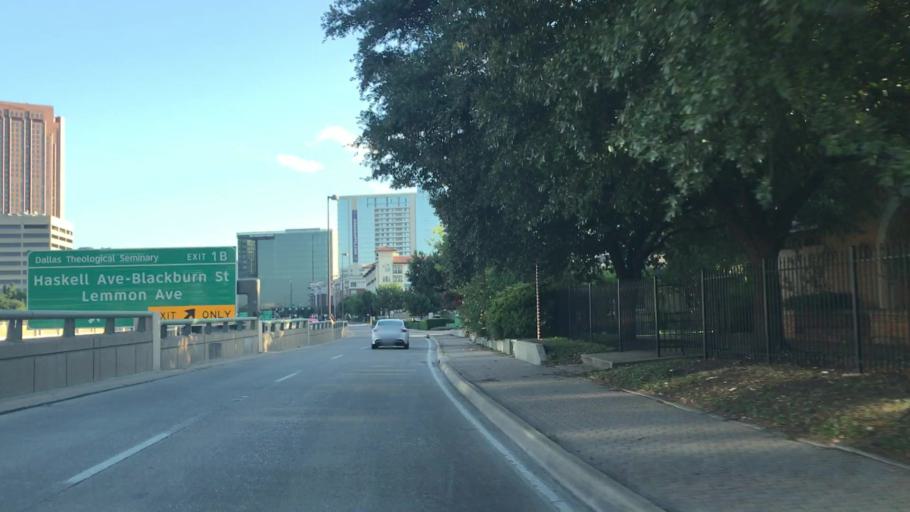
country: US
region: Texas
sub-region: Dallas County
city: Highland Park
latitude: 32.8121
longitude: -96.7916
